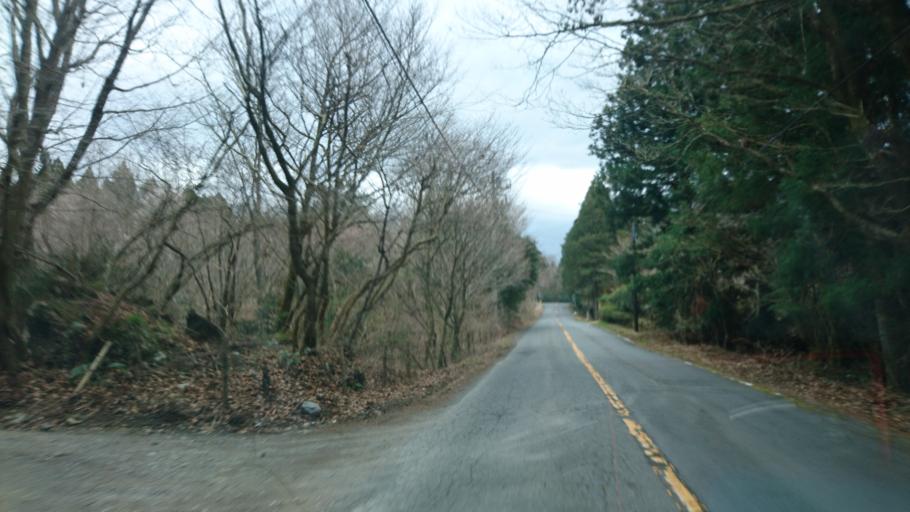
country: JP
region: Shizuoka
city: Fujinomiya
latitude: 35.3504
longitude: 138.5703
